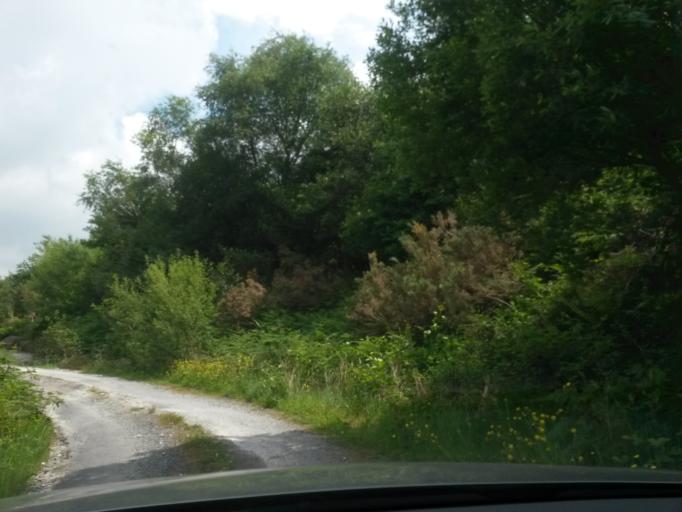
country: IE
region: Munster
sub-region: Ciarrai
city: Kenmare
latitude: 51.8154
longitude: -9.5228
